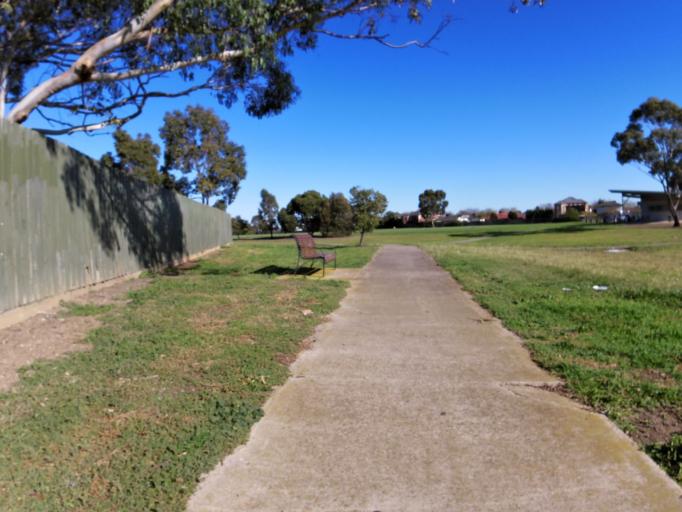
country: AU
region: Victoria
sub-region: Wyndham
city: Tarneit
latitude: -37.8685
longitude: 144.6776
